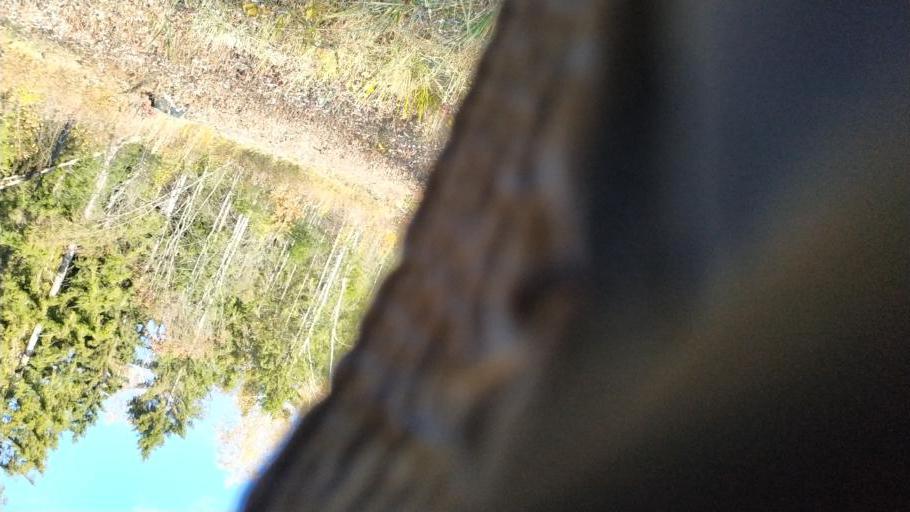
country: RU
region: Moskovskaya
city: Lobnya
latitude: 55.9985
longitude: 37.4628
